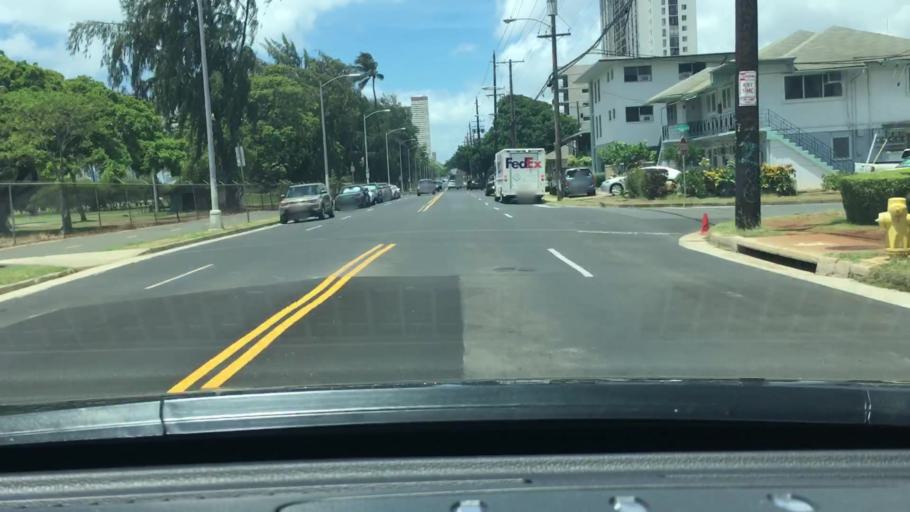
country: US
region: Hawaii
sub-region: Honolulu County
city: Honolulu
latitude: 21.2797
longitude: -157.8146
